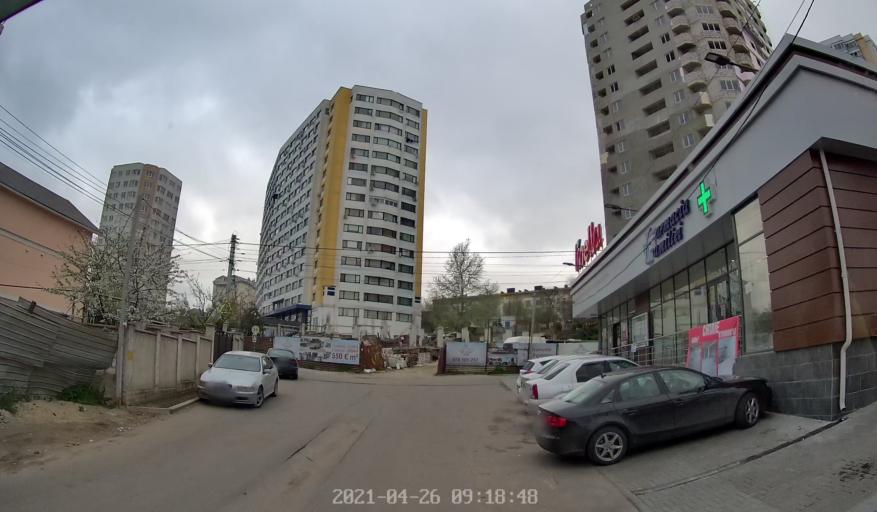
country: MD
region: Chisinau
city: Stauceni
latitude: 47.0944
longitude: 28.8694
